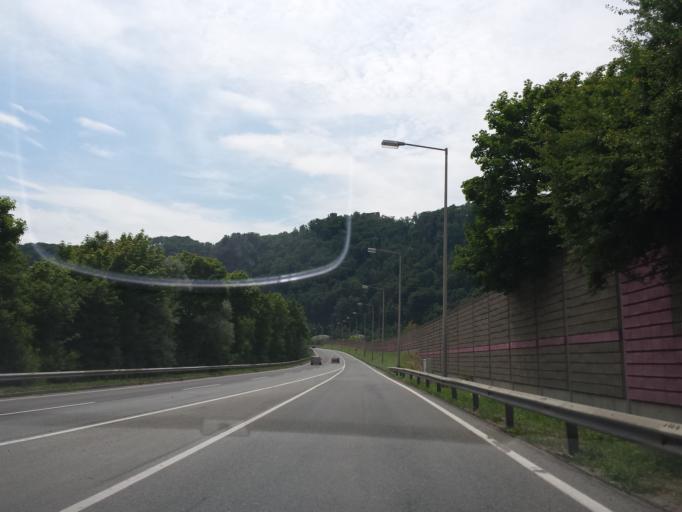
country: AT
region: Styria
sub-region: Graz Stadt
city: Goesting
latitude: 47.1114
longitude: 15.3755
